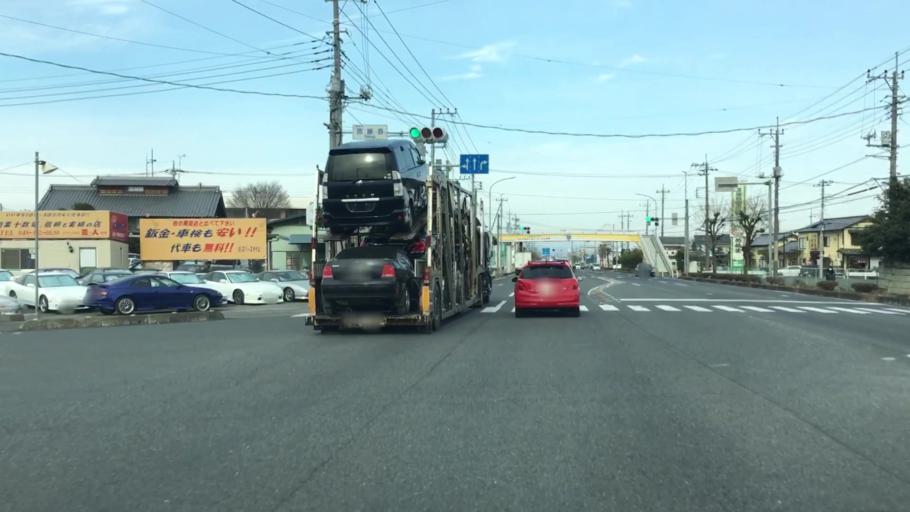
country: JP
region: Saitama
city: Menuma
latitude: 36.2220
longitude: 139.3688
